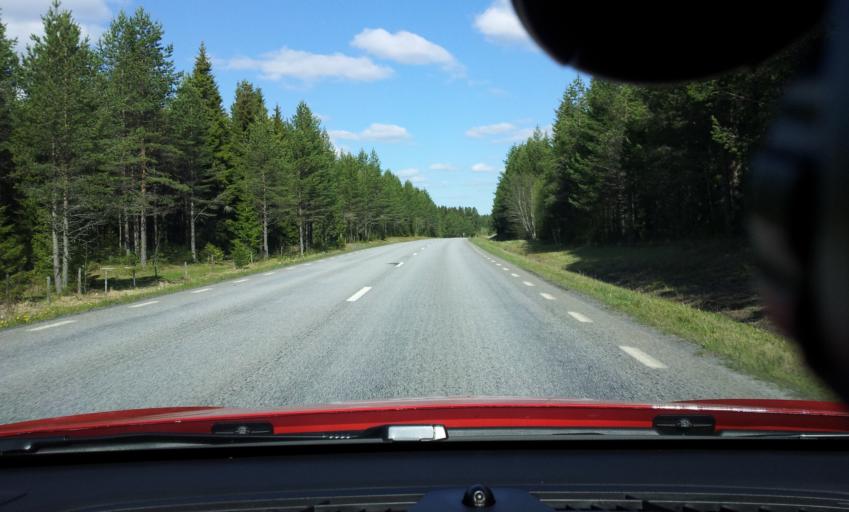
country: SE
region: Jaemtland
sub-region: Krokoms Kommun
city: Valla
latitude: 63.2720
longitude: 13.9496
